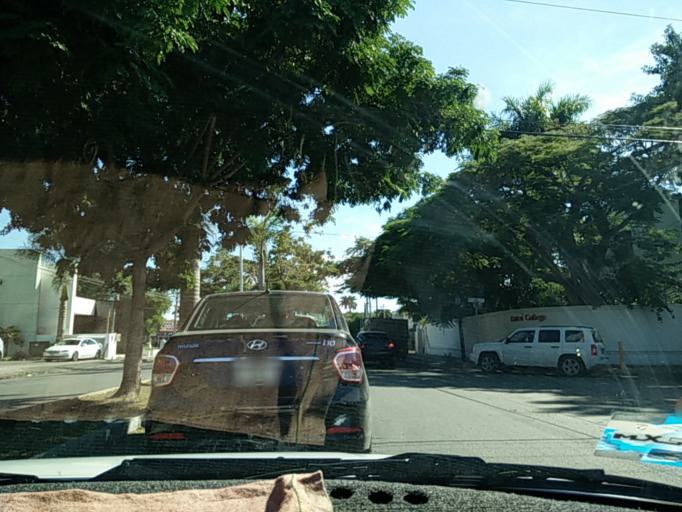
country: MX
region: Yucatan
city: Merida
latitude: 20.9981
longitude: -89.6122
